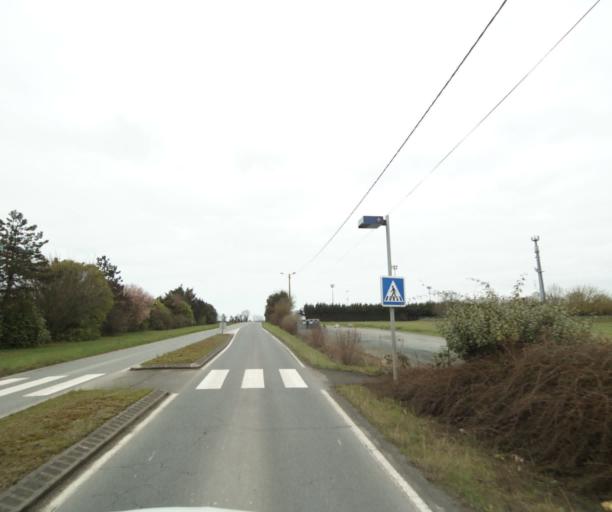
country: FR
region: Poitou-Charentes
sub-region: Departement de la Charente-Maritime
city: Lagord
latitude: 46.1946
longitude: -1.1528
